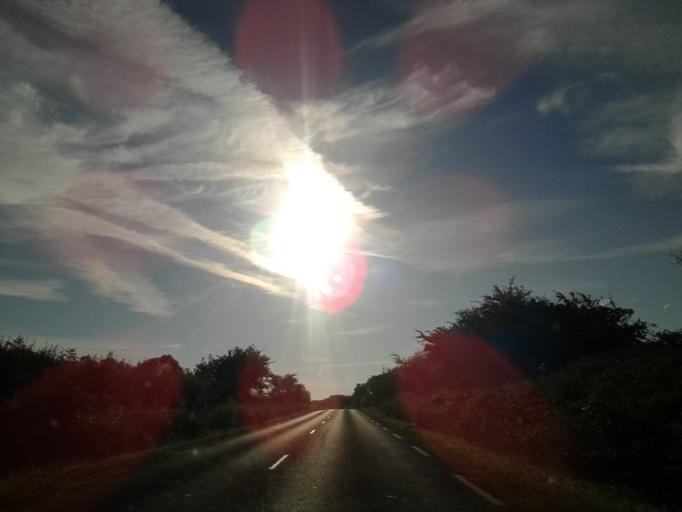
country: FR
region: Lower Normandy
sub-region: Departement de la Manche
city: Fermanville
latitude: 49.6459
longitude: -1.4488
